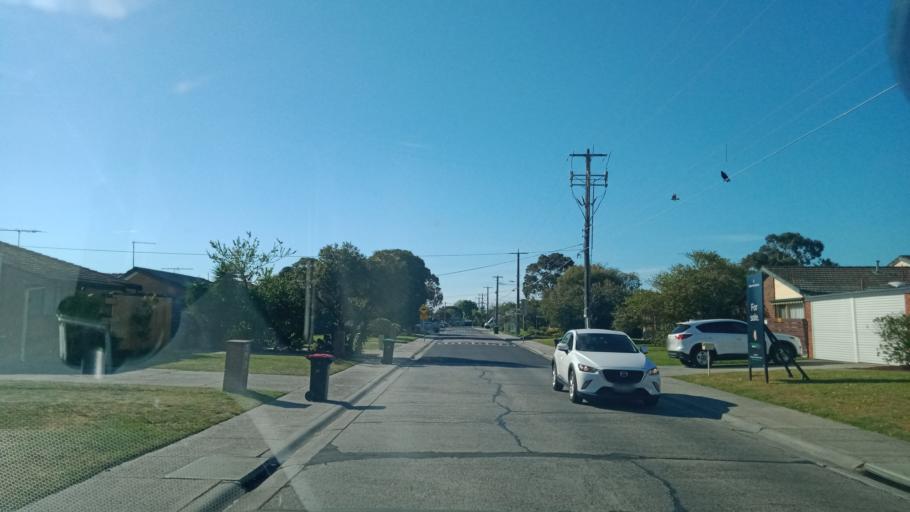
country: AU
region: Victoria
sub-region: Kingston
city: Chelsea
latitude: -38.0454
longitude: 145.1226
